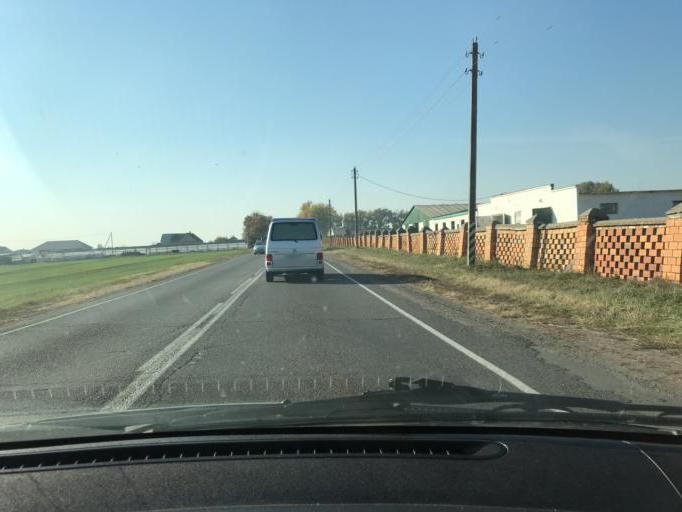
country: BY
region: Brest
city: Davyd-Haradok
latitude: 52.0612
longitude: 27.2969
